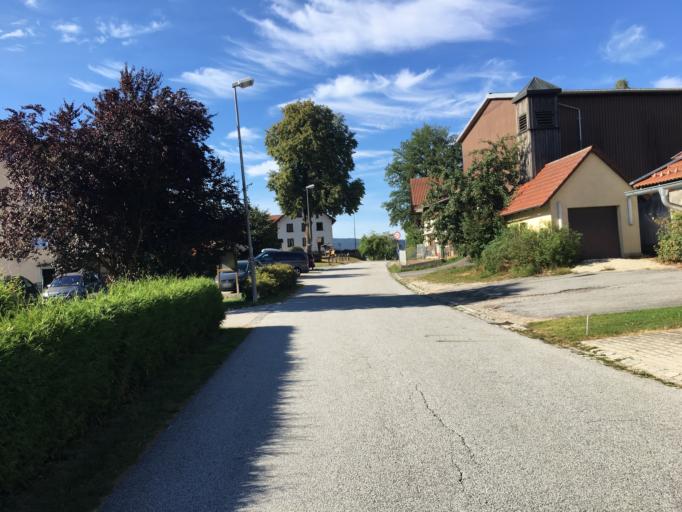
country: DE
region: Bavaria
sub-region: Lower Bavaria
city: Zwiesel
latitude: 48.9954
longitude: 13.2201
